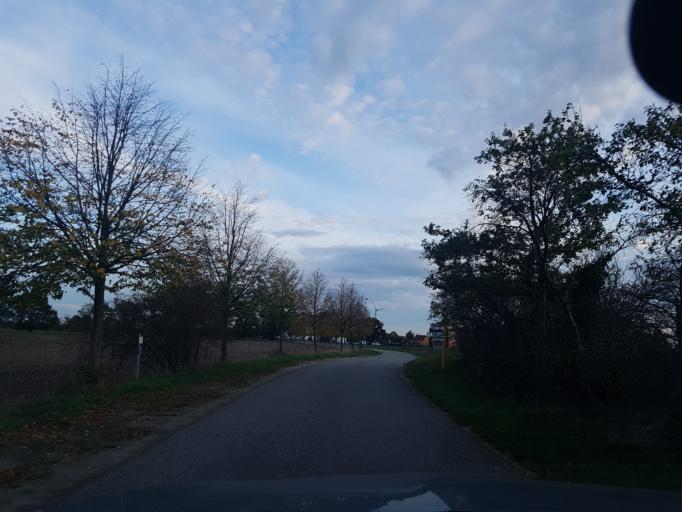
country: DE
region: Brandenburg
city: Elsterwerda
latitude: 51.4600
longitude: 13.4657
